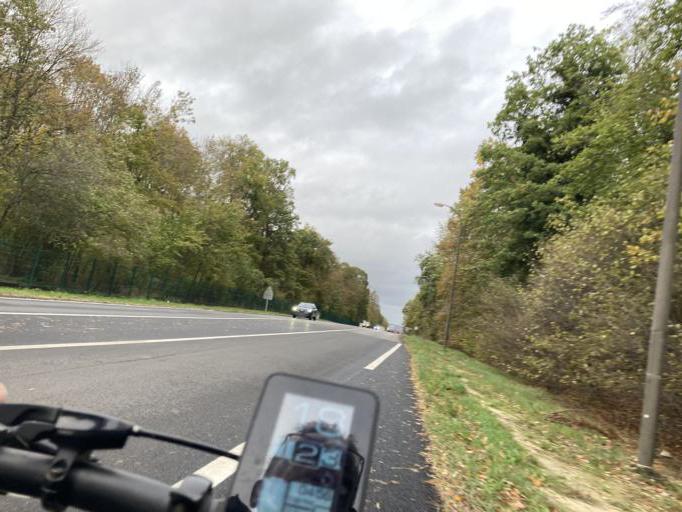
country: FR
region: Picardie
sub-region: Departement de l'Oise
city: Lamorlaye
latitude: 49.1671
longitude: 2.4486
